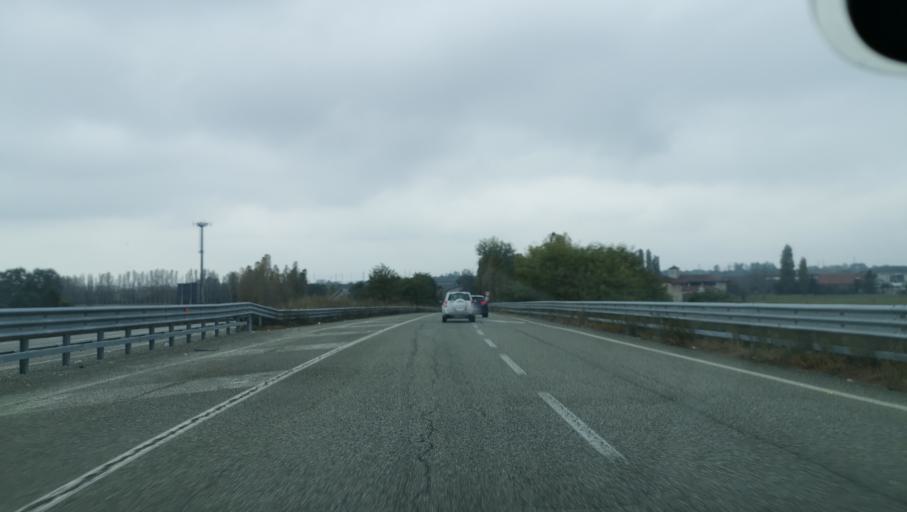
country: IT
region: Piedmont
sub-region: Provincia di Torino
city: Brandizzo
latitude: 45.1679
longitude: 7.8138
